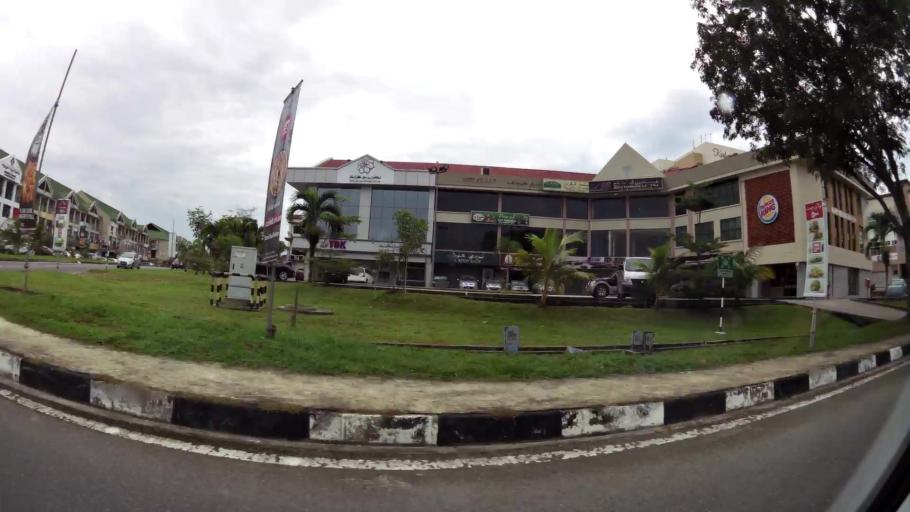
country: BN
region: Brunei and Muara
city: Bandar Seri Begawan
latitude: 4.9020
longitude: 114.9278
